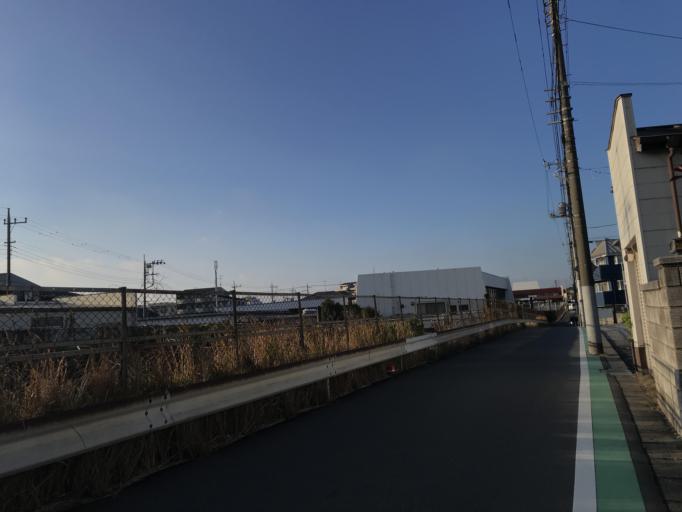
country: JP
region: Chiba
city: Funabashi
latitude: 35.7291
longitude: 139.9677
